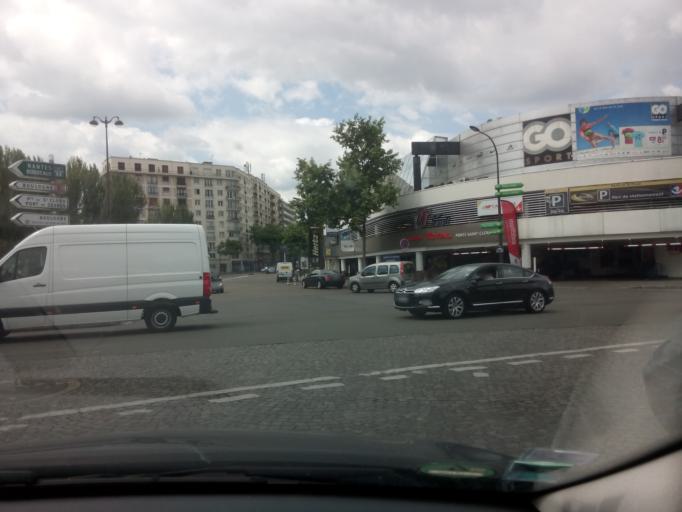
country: FR
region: Ile-de-France
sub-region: Departement des Hauts-de-Seine
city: Boulogne-Billancourt
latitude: 48.8385
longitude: 2.2543
